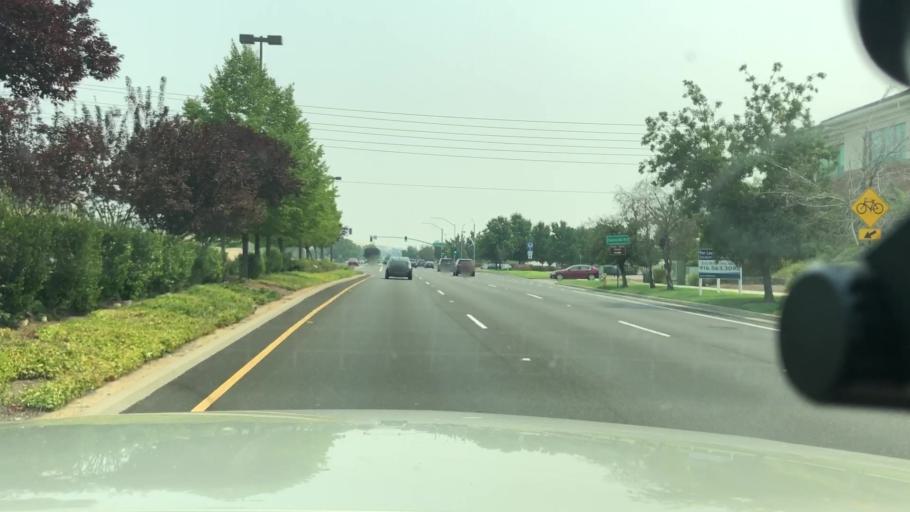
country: US
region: California
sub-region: Sacramento County
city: Folsom
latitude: 38.6593
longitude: -121.1299
